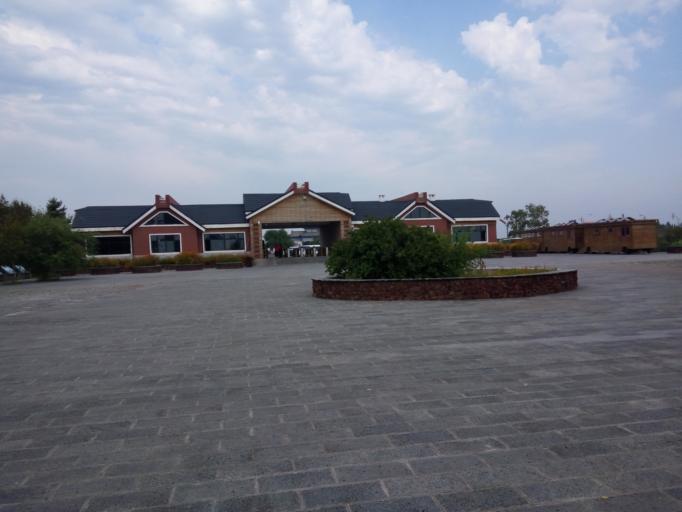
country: CN
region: Heilongjiang Sheng
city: Erjing
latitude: 48.6479
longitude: 126.1490
